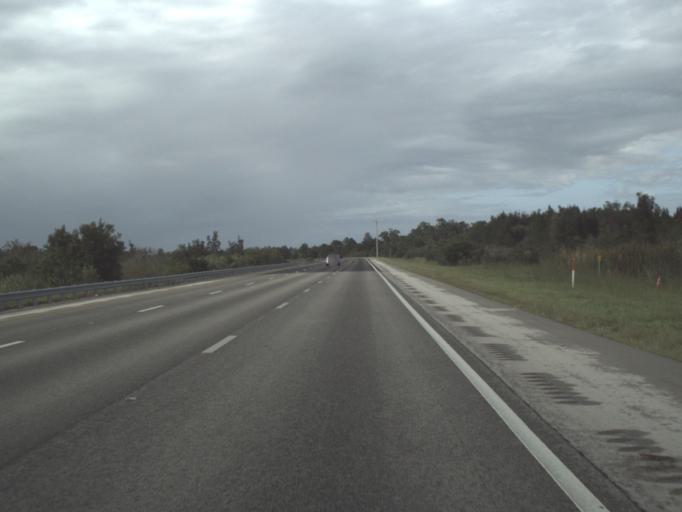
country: US
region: Florida
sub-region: Lee County
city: Suncoast Estates
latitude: 26.7651
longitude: -81.8755
